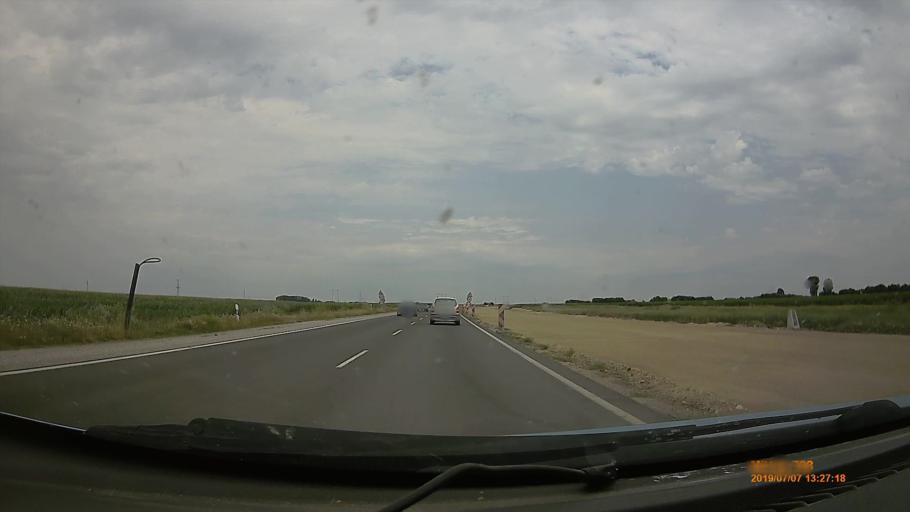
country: HU
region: Pest
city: Abony
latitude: 47.2191
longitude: 19.9888
